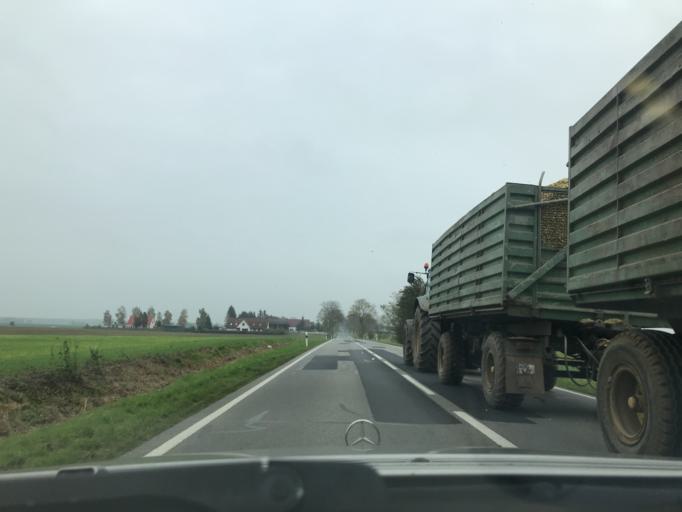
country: DE
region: Mecklenburg-Vorpommern
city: Wusterhusen
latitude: 54.1007
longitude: 13.6761
